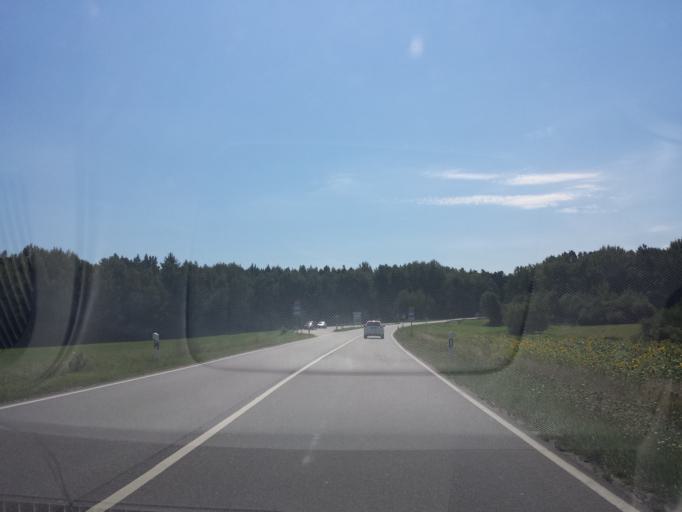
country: DE
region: Bavaria
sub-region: Upper Palatinate
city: Traitsching
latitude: 49.1851
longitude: 12.6531
